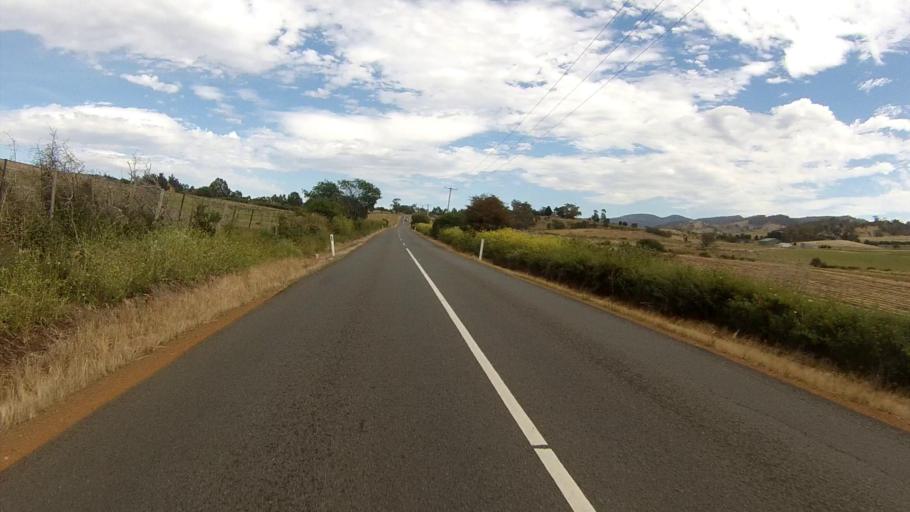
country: AU
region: Tasmania
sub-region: Brighton
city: Old Beach
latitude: -42.7024
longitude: 147.3629
